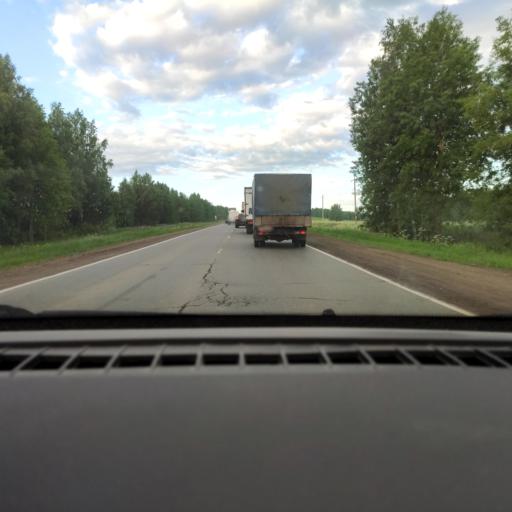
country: RU
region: Perm
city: Nytva
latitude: 57.9706
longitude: 55.1774
